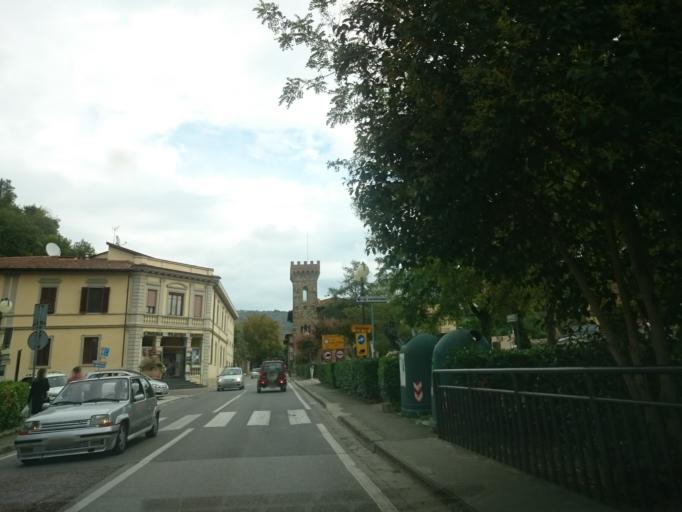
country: IT
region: Tuscany
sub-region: Province of Florence
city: Greve in Chianti
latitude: 43.5830
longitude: 11.3183
